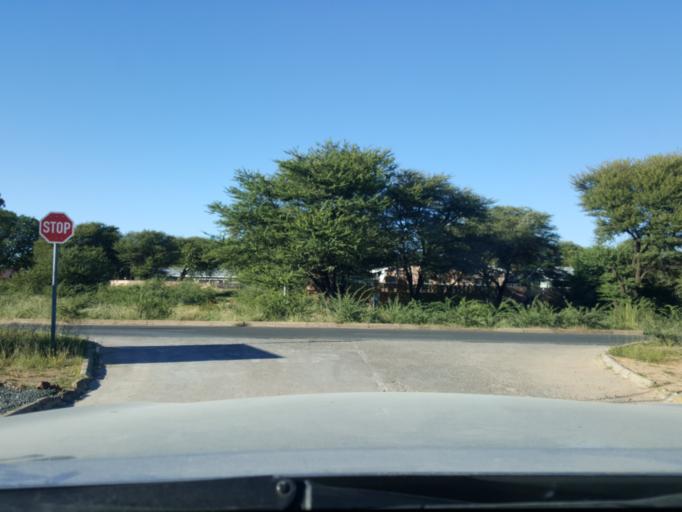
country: BW
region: Kweneng
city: Letlhakeng
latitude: -24.5932
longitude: 24.7256
